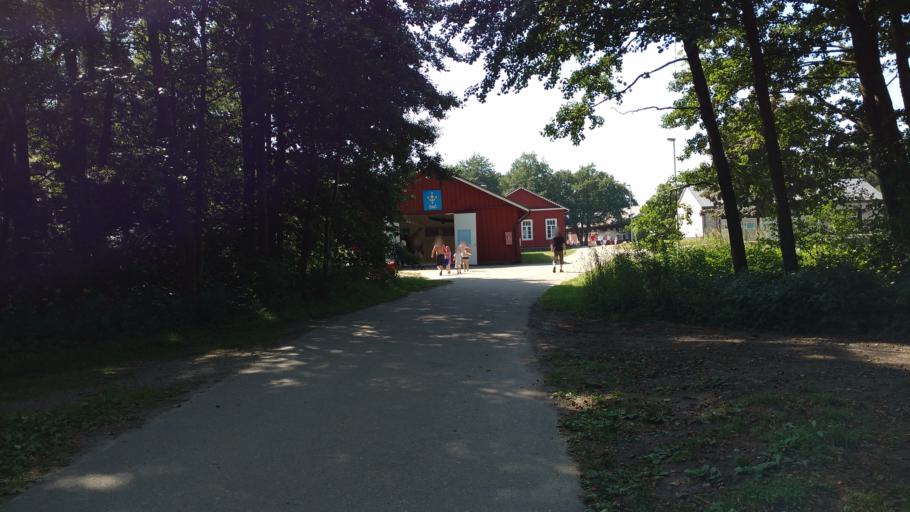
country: FI
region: Varsinais-Suomi
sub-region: Aboland-Turunmaa
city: Dragsfjaerd
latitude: 59.8077
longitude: 22.3376
